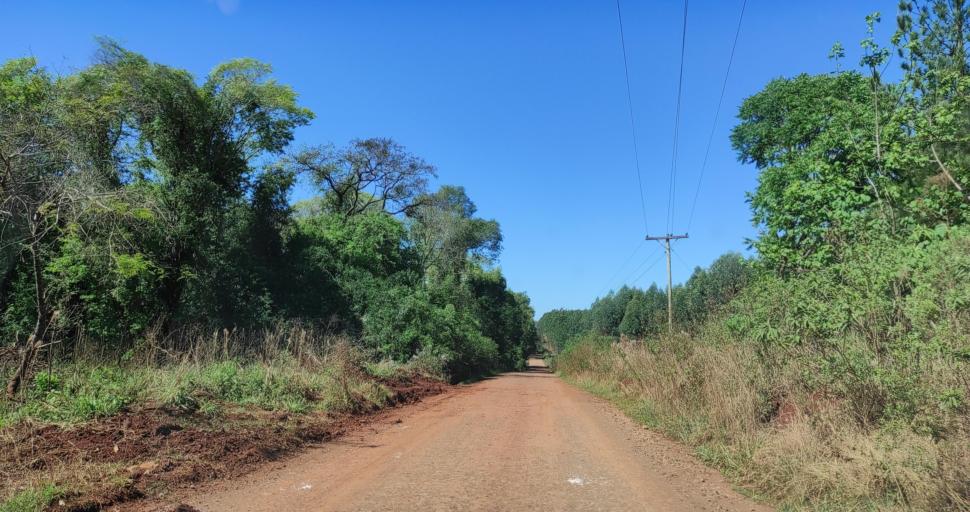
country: AR
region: Misiones
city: Capiovi
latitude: -26.9351
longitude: -55.0297
